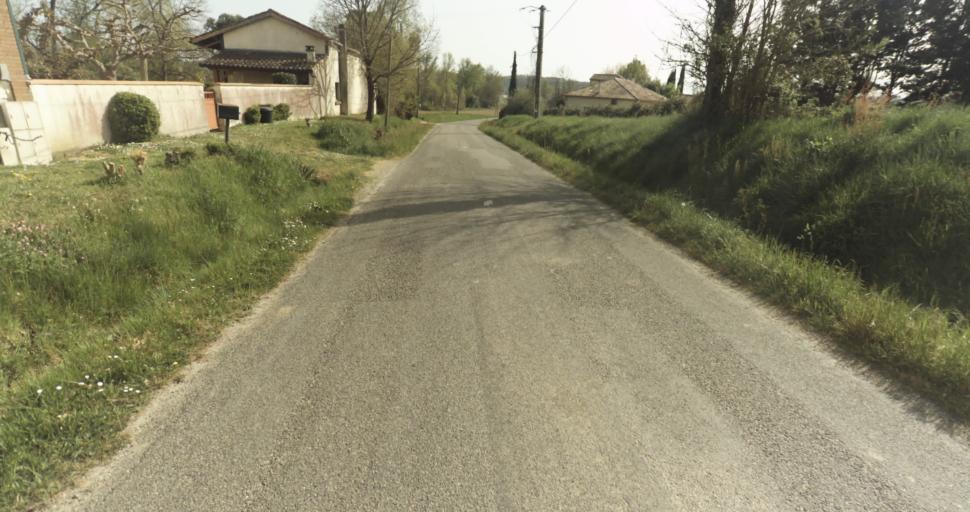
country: FR
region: Midi-Pyrenees
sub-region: Departement du Tarn-et-Garonne
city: Lafrancaise
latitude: 44.1415
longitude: 1.1754
